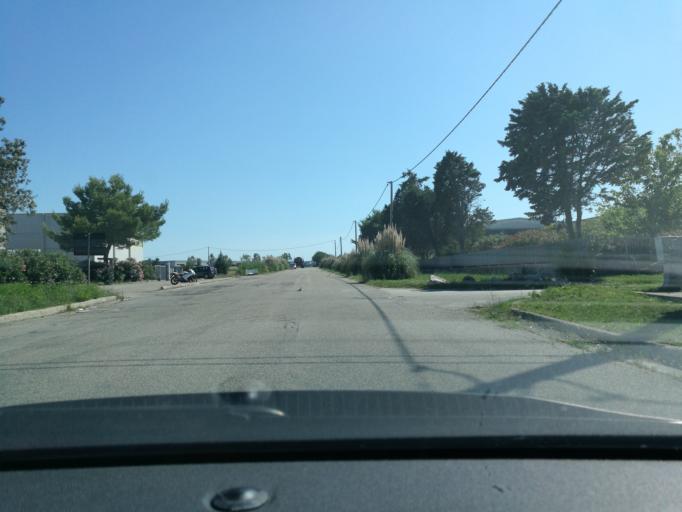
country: IT
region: Abruzzo
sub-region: Provincia di Chieti
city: Vasto
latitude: 42.1715
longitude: 14.6967
